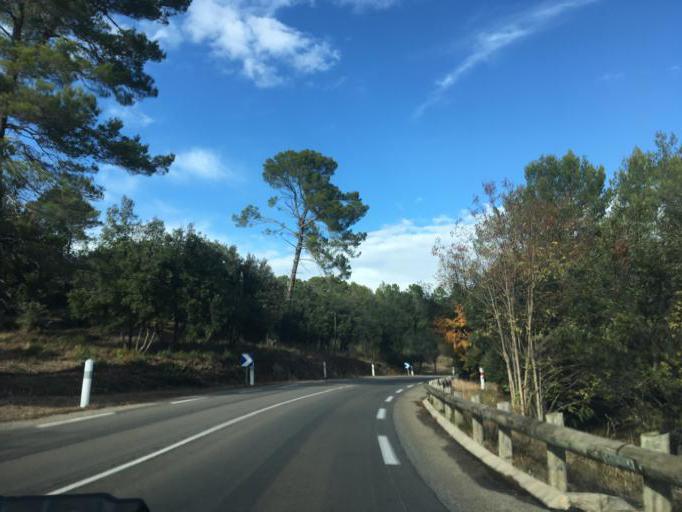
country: FR
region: Provence-Alpes-Cote d'Azur
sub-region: Departement du Var
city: Lorgues
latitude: 43.5142
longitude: 6.3383
